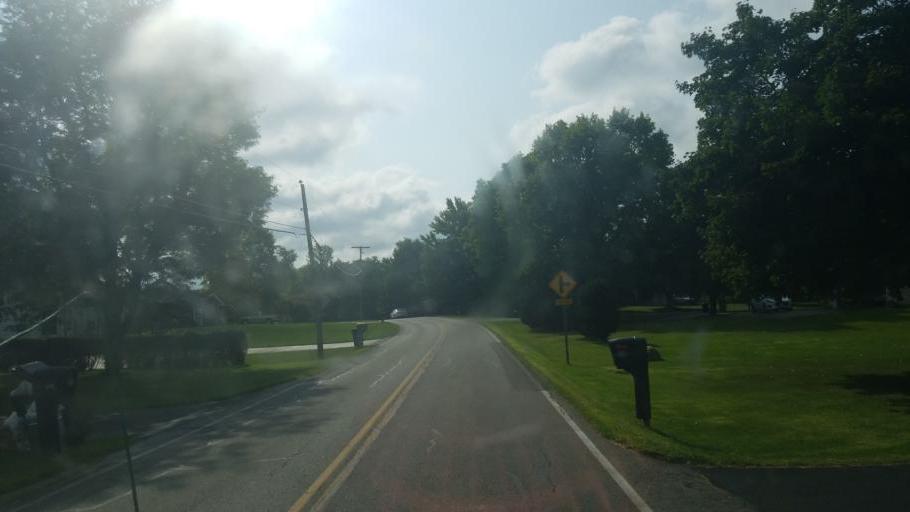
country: US
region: Ohio
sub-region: Marion County
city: Marion
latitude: 40.5702
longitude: -83.0817
